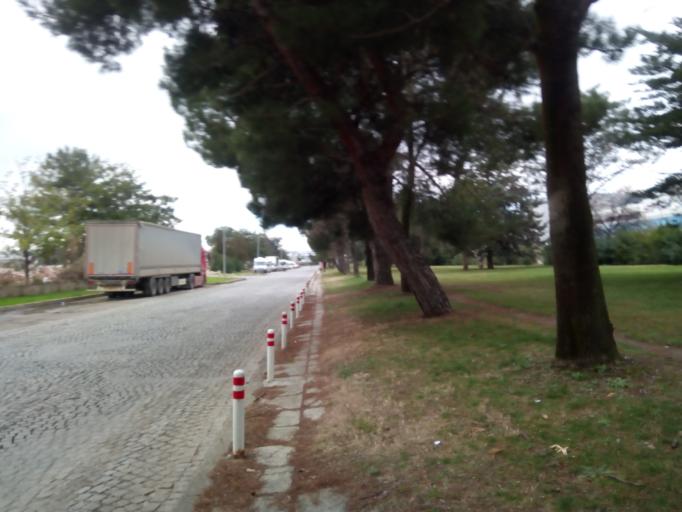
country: TR
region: Bursa
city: Niluefer
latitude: 40.2480
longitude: 28.9600
